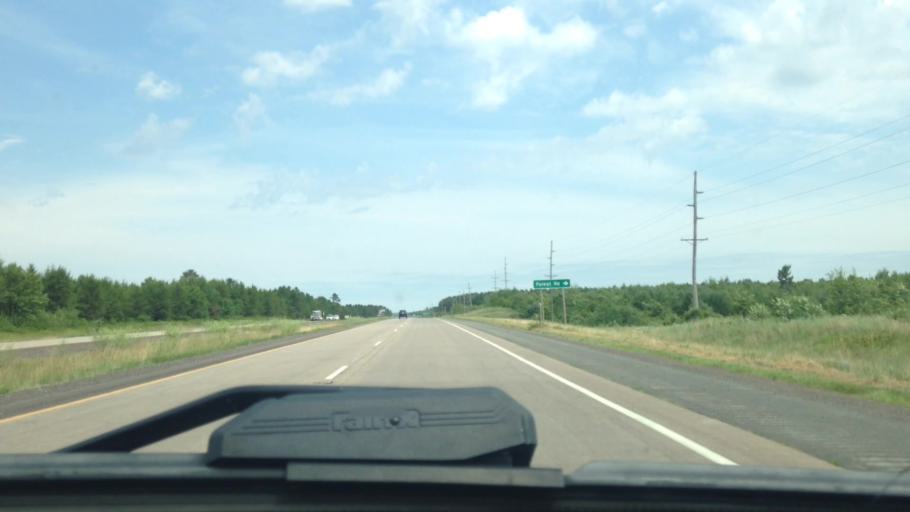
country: US
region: Wisconsin
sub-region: Douglas County
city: Lake Nebagamon
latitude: 46.2951
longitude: -91.8113
